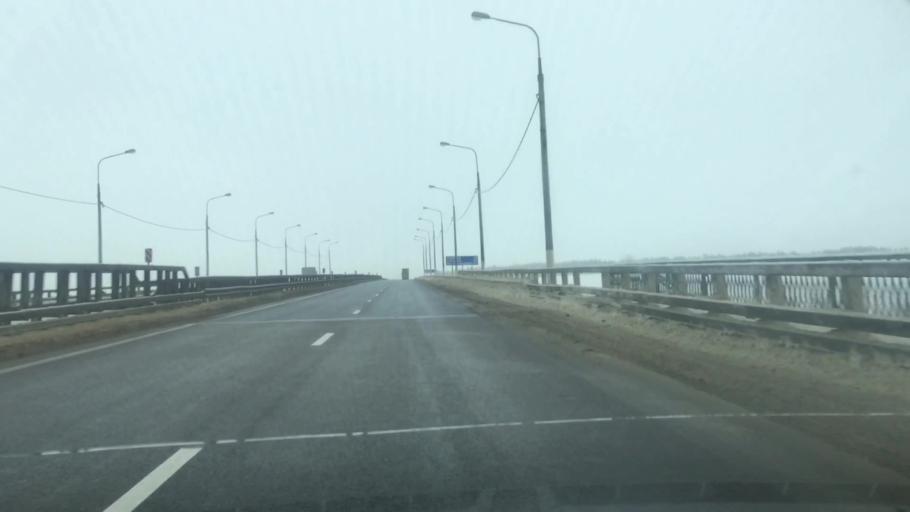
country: RU
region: Lipetsk
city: Stanovoye
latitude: 52.7954
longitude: 38.3287
